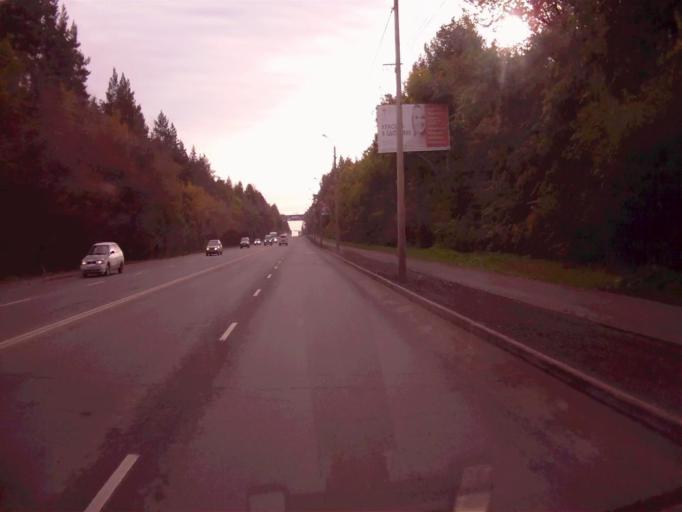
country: RU
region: Chelyabinsk
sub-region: Gorod Chelyabinsk
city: Chelyabinsk
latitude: 55.1468
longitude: 61.3435
